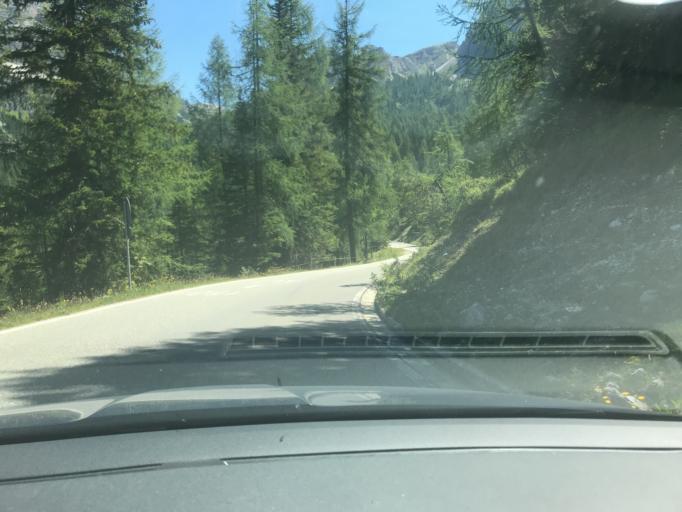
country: IT
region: Trentino-Alto Adige
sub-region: Bolzano
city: Sesto
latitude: 46.6008
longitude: 12.2703
